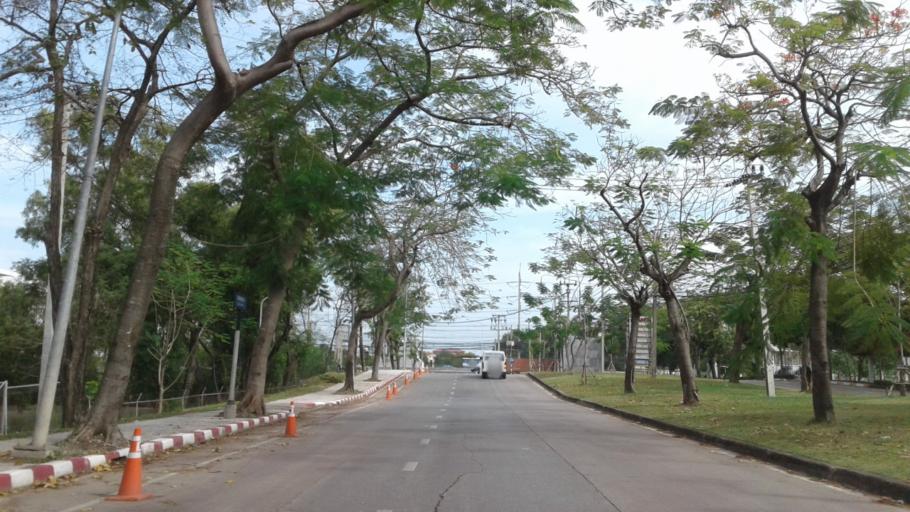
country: TH
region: Pathum Thani
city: Khlong Luang
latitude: 14.0759
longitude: 100.6160
